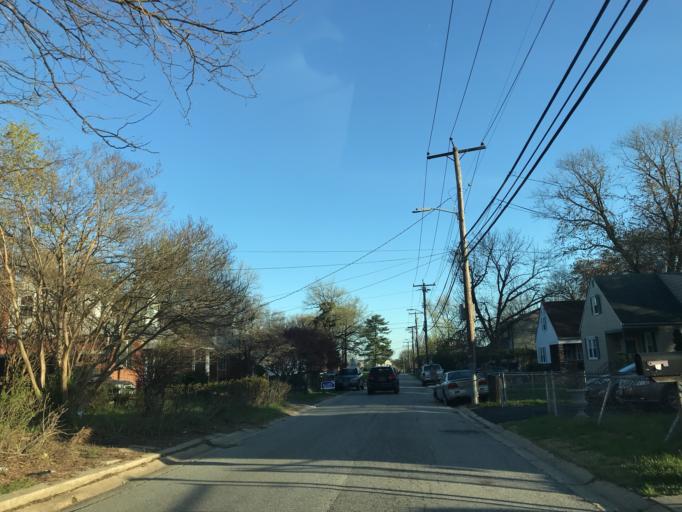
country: US
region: Maryland
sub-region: Baltimore County
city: Rosedale
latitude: 39.3397
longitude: -76.5345
